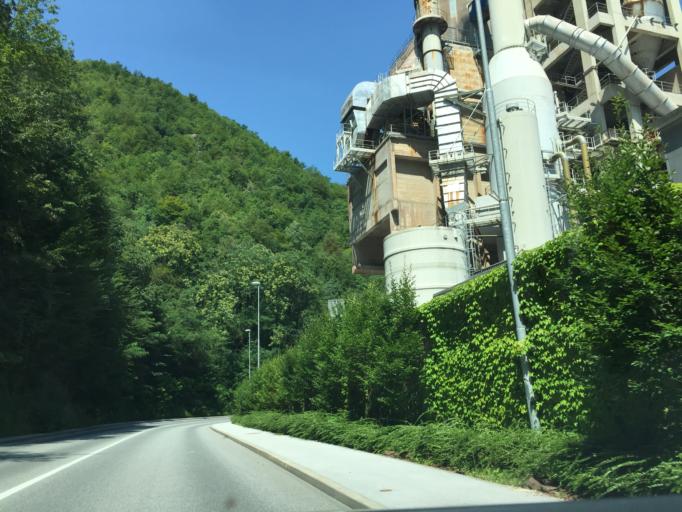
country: SI
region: Trbovlje
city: Trbovlje
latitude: 46.1284
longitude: 15.0341
